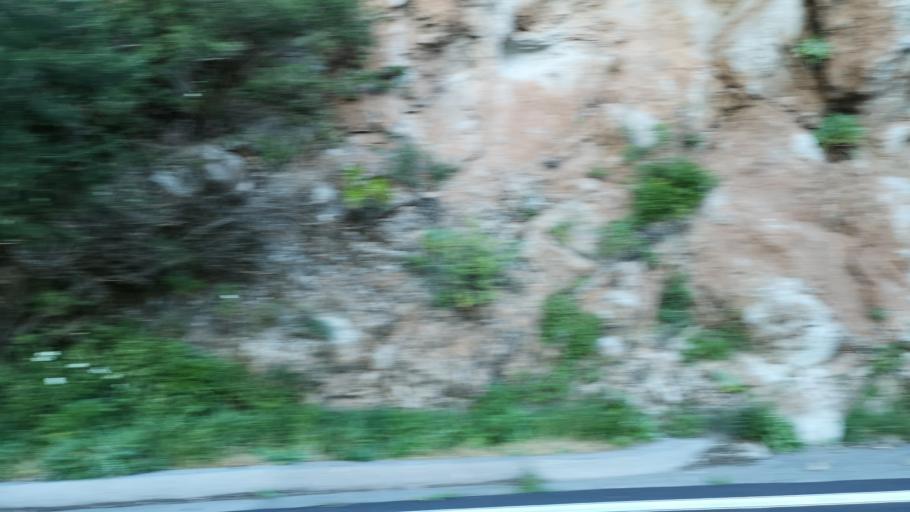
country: ES
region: Canary Islands
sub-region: Provincia de Santa Cruz de Tenerife
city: Alajero
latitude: 28.0887
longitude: -17.2515
